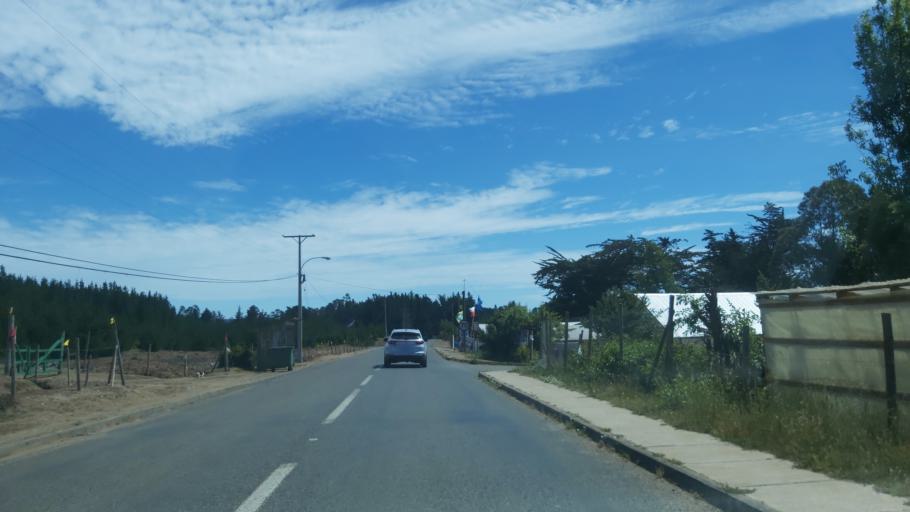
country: CL
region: Maule
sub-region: Provincia de Talca
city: Constitucion
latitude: -35.5105
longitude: -72.5247
